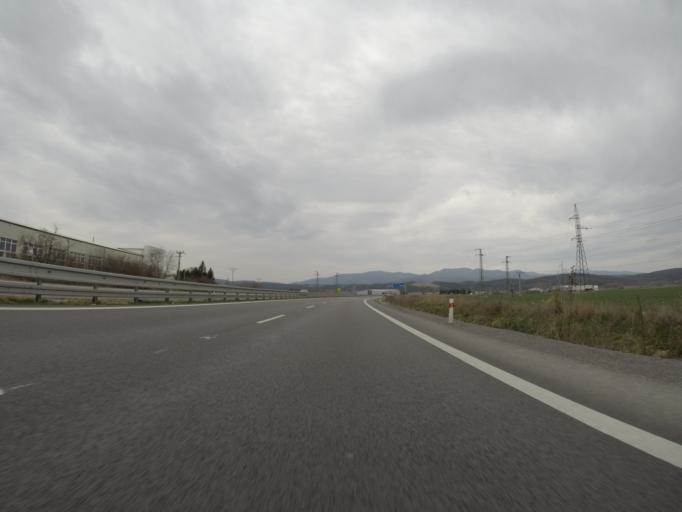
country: SK
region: Nitriansky
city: Novaky
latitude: 48.7206
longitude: 18.5615
